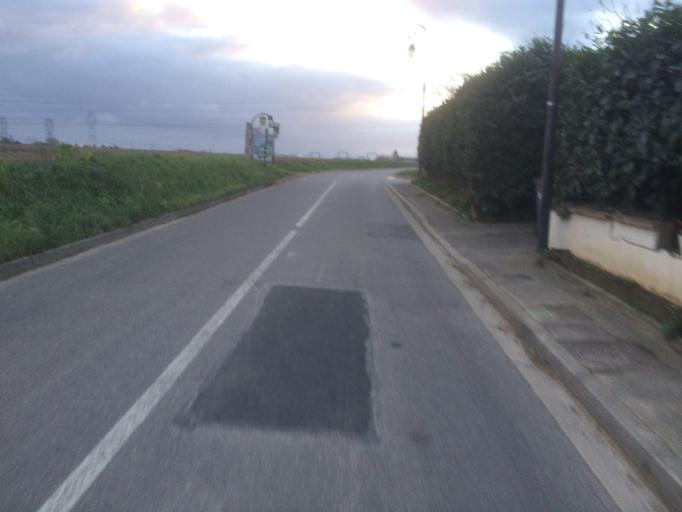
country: FR
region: Ile-de-France
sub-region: Departement de l'Essonne
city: Villejust
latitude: 48.6700
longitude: 2.2119
